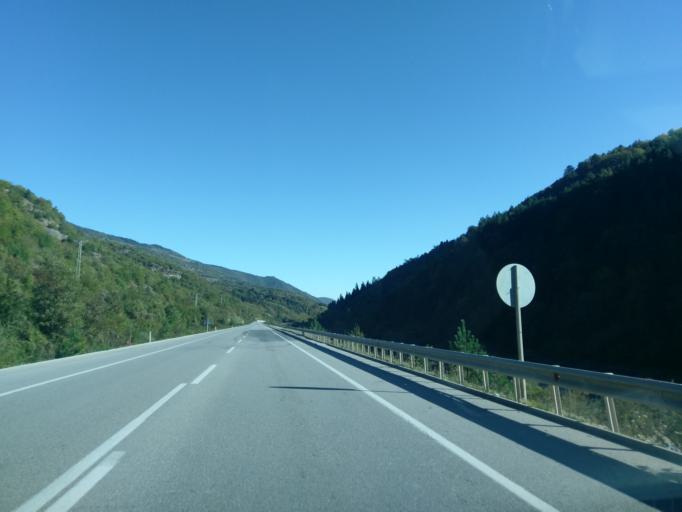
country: TR
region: Sinop
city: Erfelek
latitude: 41.7151
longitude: 34.9344
